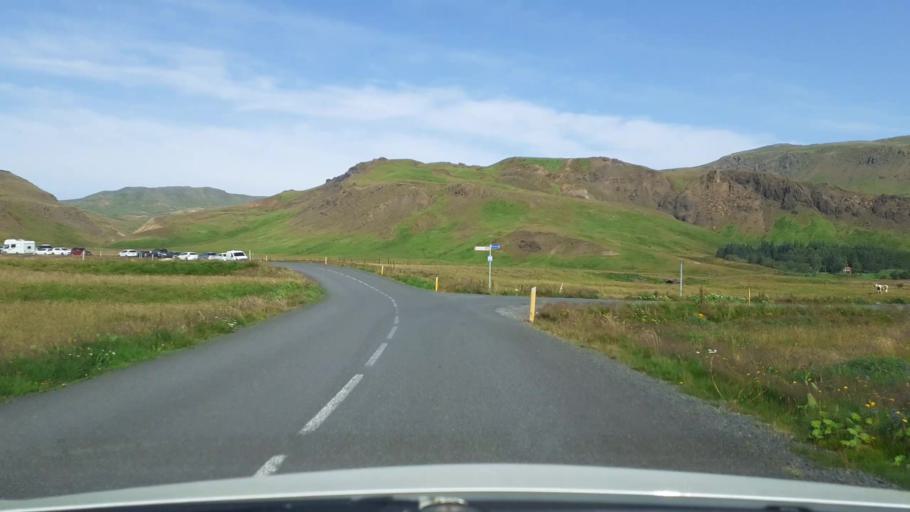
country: IS
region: South
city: Hveragerdi
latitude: 64.0179
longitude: -21.2082
